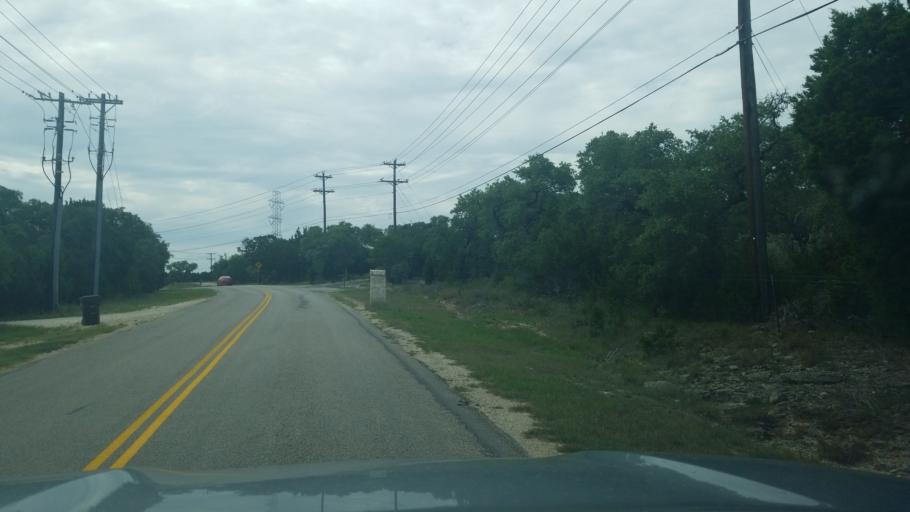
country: US
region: Texas
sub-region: Comal County
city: Bulverde
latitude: 29.7796
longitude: -98.4139
